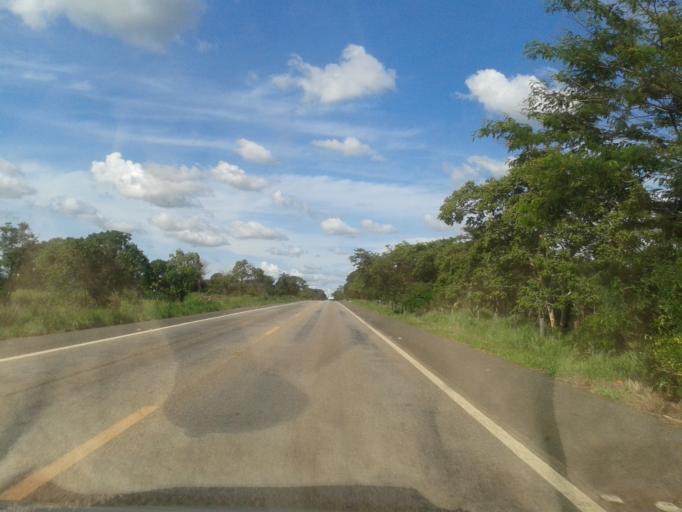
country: BR
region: Goias
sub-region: Mozarlandia
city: Mozarlandia
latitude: -15.0605
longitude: -50.6137
